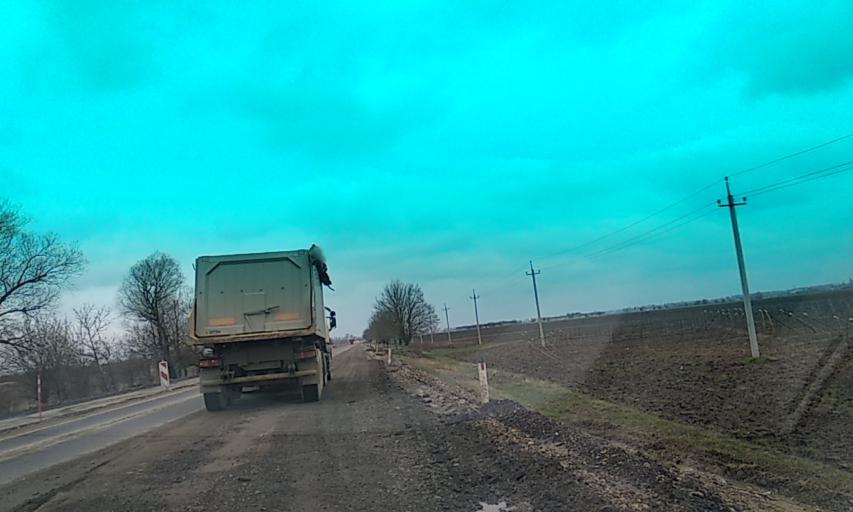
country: RU
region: Krasnodarskiy
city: Velikovechnoye
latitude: 44.9966
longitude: 39.7102
